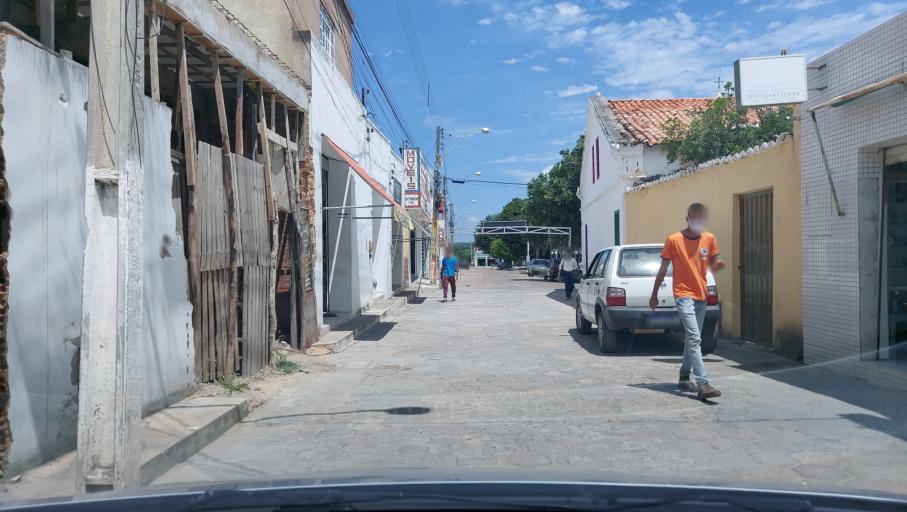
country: BR
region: Bahia
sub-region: Oliveira Dos Brejinhos
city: Beira Rio
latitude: -11.9996
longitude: -42.6266
